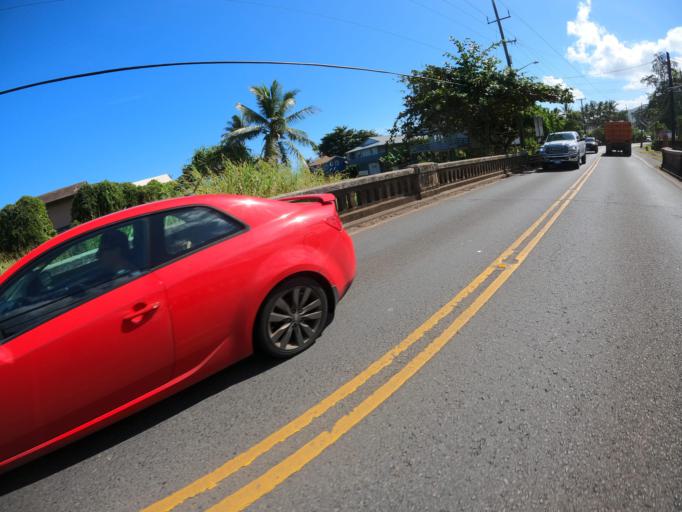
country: US
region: Hawaii
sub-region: Honolulu County
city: Hau'ula
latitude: 21.6172
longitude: -157.9140
